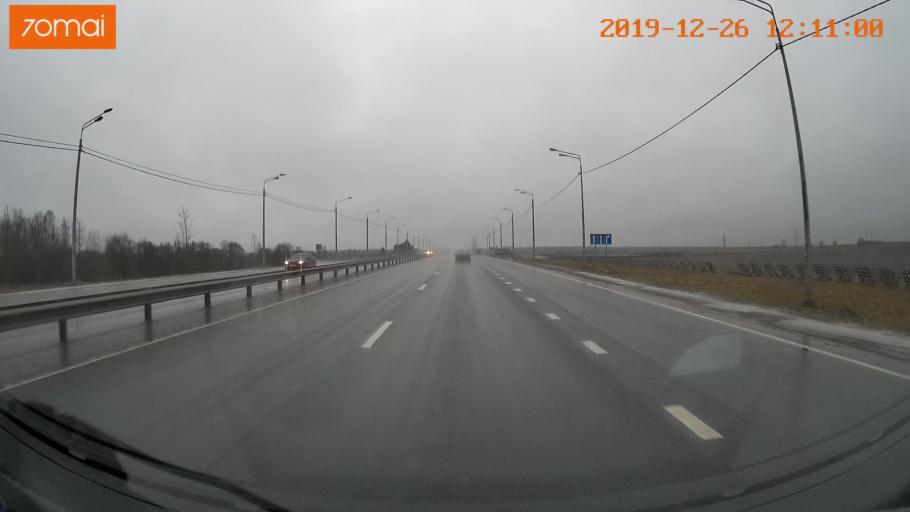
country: RU
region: Vologda
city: Tonshalovo
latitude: 59.2531
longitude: 37.9748
